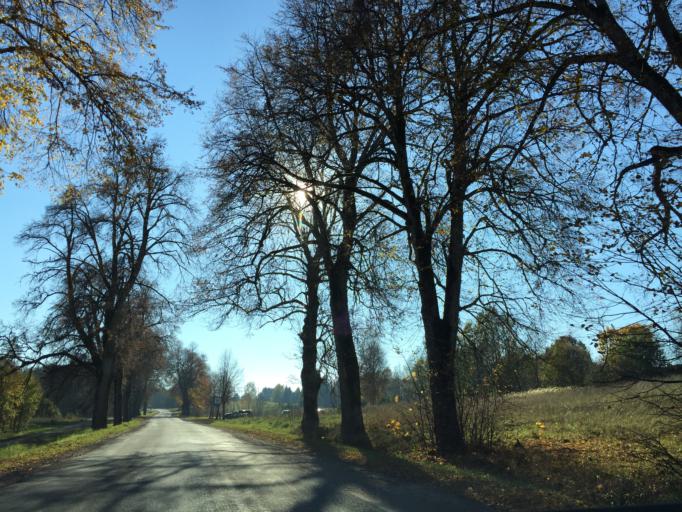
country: LT
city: Plateliai
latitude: 56.0328
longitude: 21.8101
